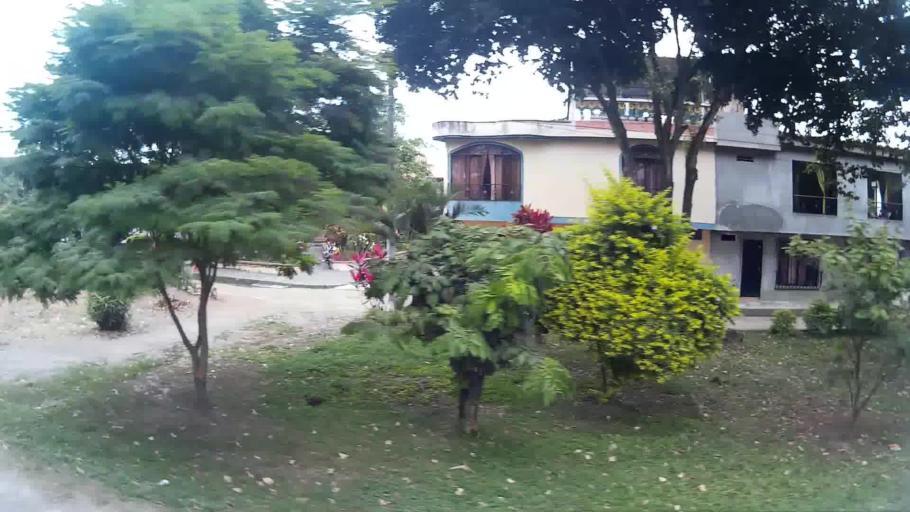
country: CO
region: Risaralda
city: La Virginia
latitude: 4.9040
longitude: -75.8783
